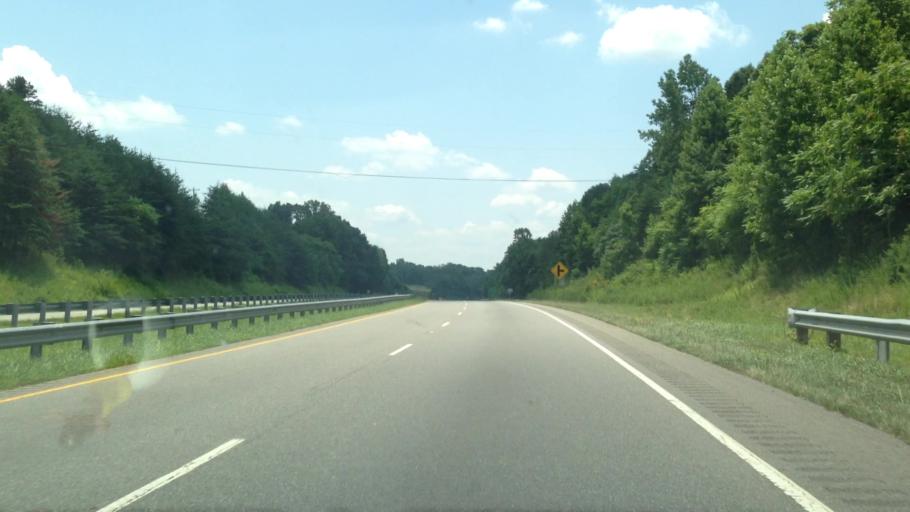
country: US
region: North Carolina
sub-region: Rockingham County
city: Stoneville
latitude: 36.5222
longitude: -79.9178
